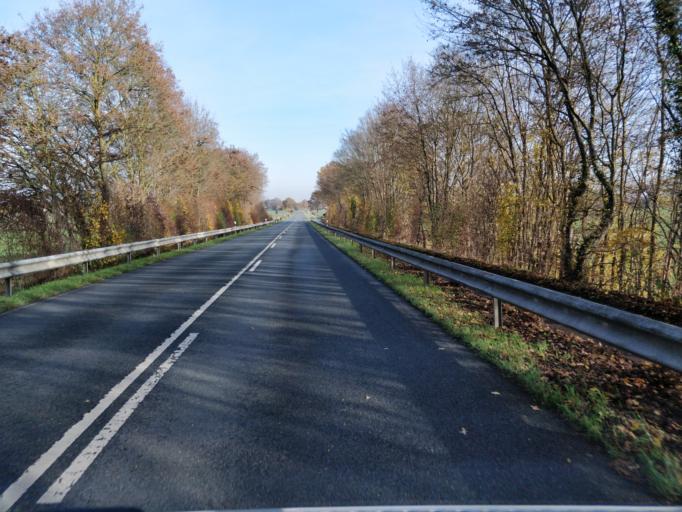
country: DE
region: North Rhine-Westphalia
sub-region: Regierungsbezirk Dusseldorf
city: Mehrhoog
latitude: 51.7287
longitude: 6.5450
